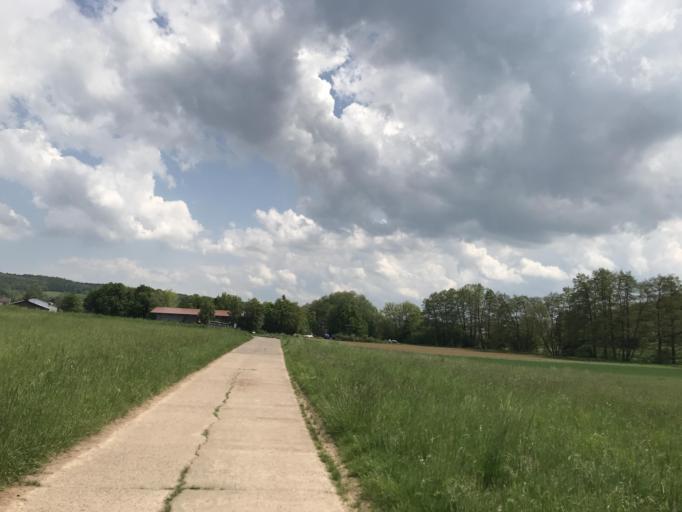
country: DE
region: Hesse
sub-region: Regierungsbezirk Darmstadt
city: Glauburg
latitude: 50.3259
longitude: 9.0351
